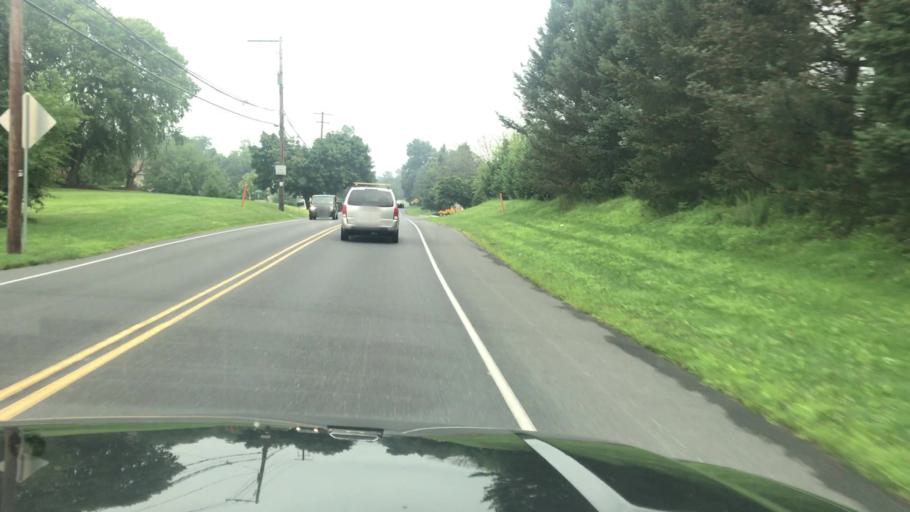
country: US
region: Pennsylvania
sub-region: Cumberland County
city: Enola
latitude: 40.2720
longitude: -76.9700
